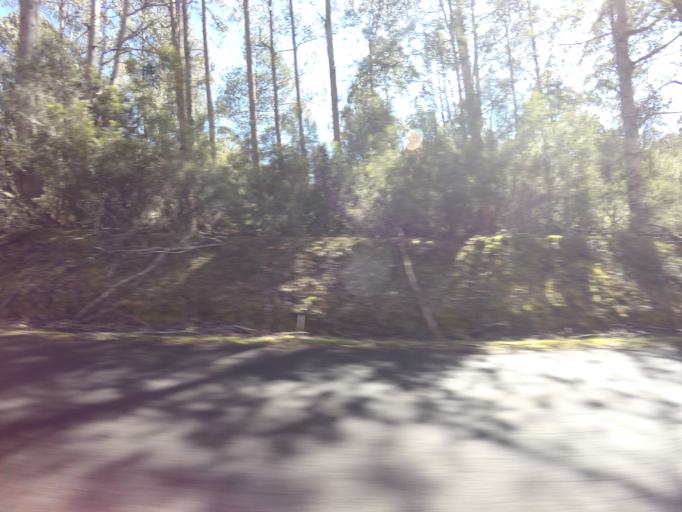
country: AU
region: Tasmania
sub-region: Derwent Valley
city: New Norfolk
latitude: -42.7500
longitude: 146.5047
